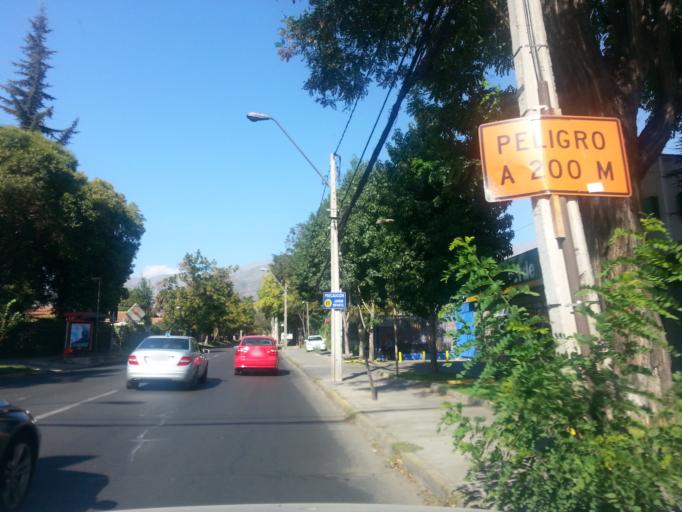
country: CL
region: Santiago Metropolitan
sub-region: Provincia de Santiago
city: Villa Presidente Frei, Nunoa, Santiago, Chile
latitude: -33.4254
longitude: -70.5524
